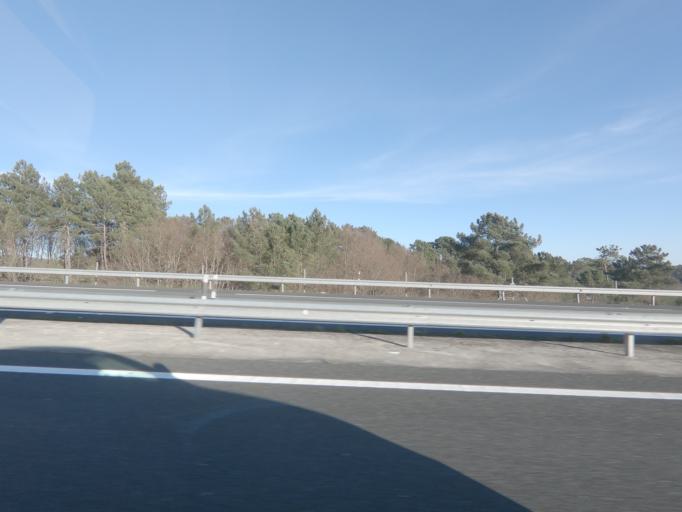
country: ES
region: Galicia
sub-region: Provincia de Ourense
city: Pinor
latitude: 42.5150
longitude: -8.0202
